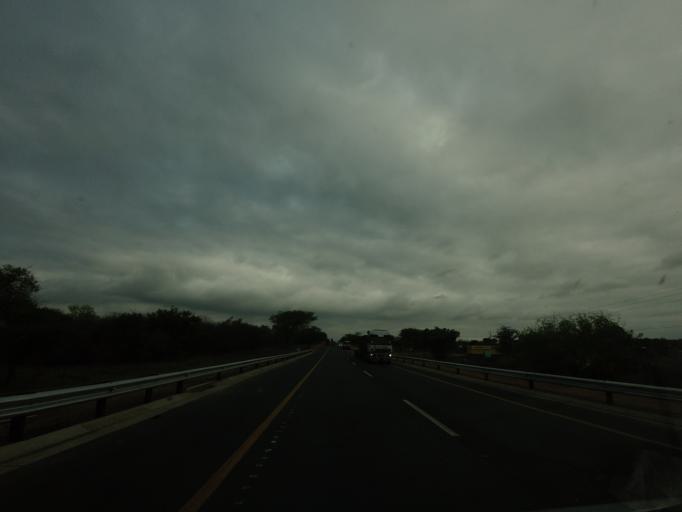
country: ZA
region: Mpumalanga
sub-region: Ehlanzeni District
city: Komatipoort
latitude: -25.4411
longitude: 31.7175
